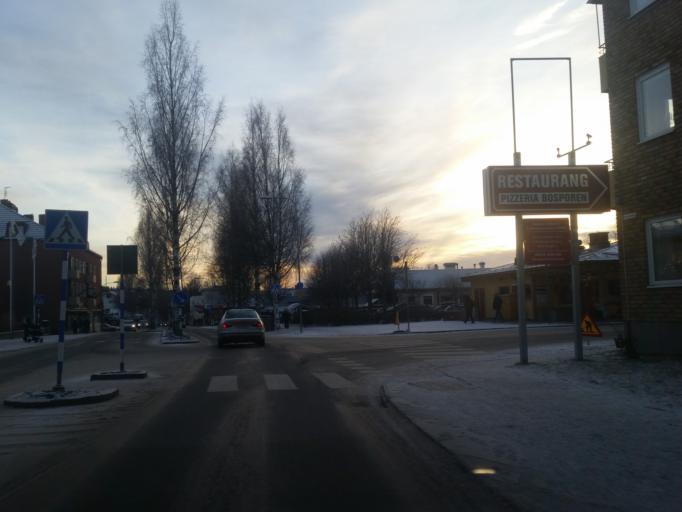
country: SE
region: Dalarna
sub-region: Leksand Municipality
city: Leksand
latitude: 60.7327
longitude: 14.9971
